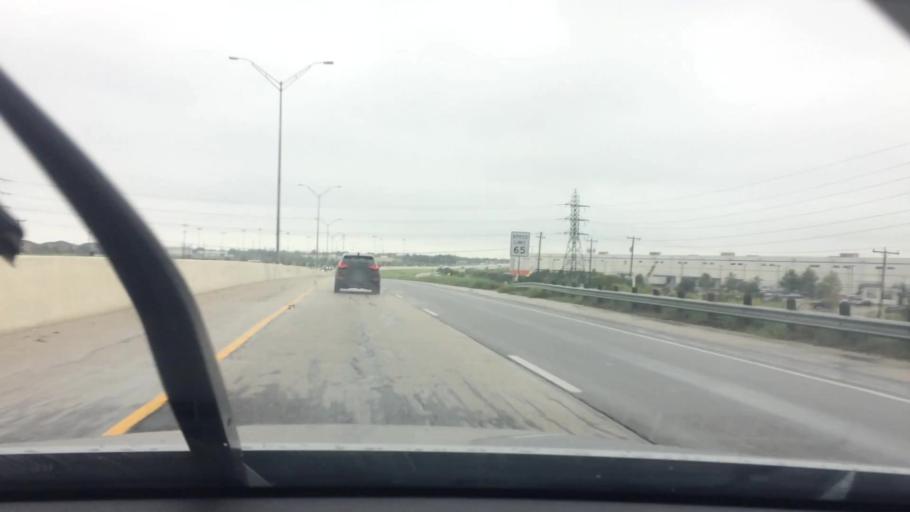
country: US
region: Texas
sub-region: Bexar County
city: Lackland Air Force Base
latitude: 29.4263
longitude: -98.5991
